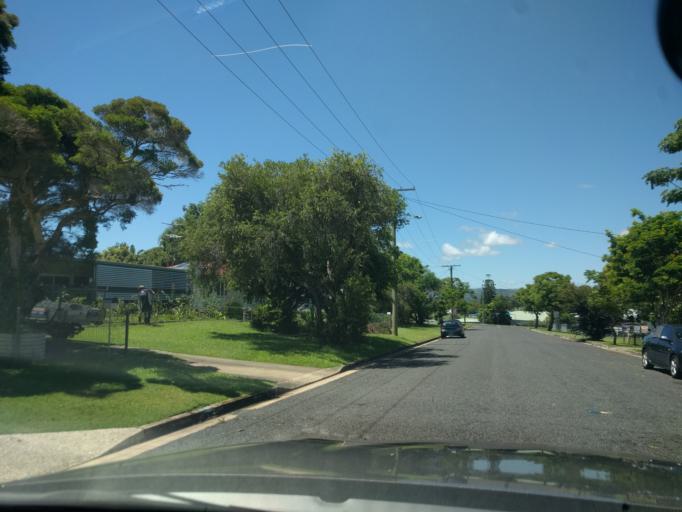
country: AU
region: Queensland
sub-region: Logan
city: Cedar Vale
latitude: -27.9864
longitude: 153.0039
